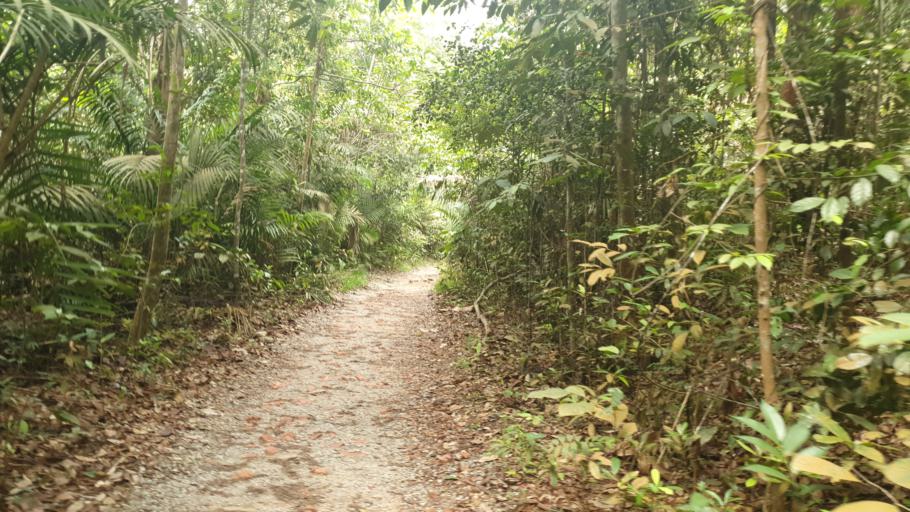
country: SG
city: Singapore
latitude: 1.3555
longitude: 103.8120
